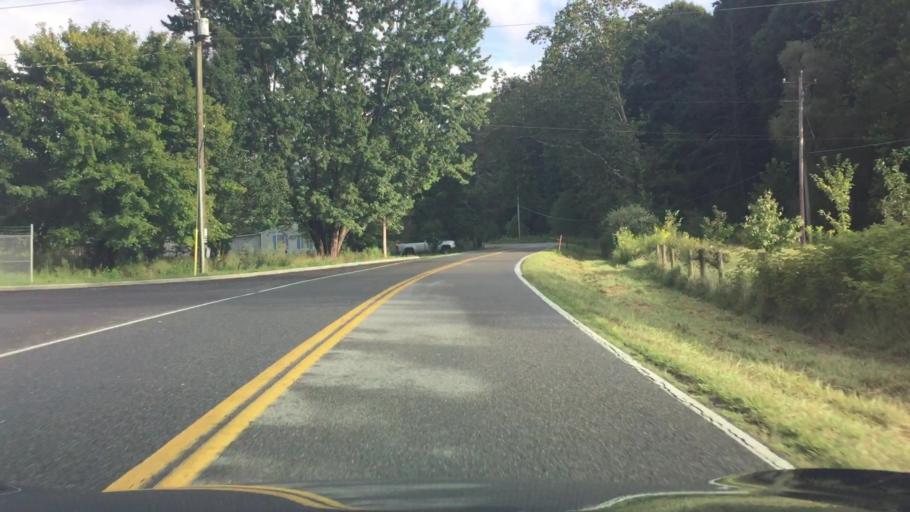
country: US
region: Virginia
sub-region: Smyth County
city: Atkins
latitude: 36.8568
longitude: -81.4303
